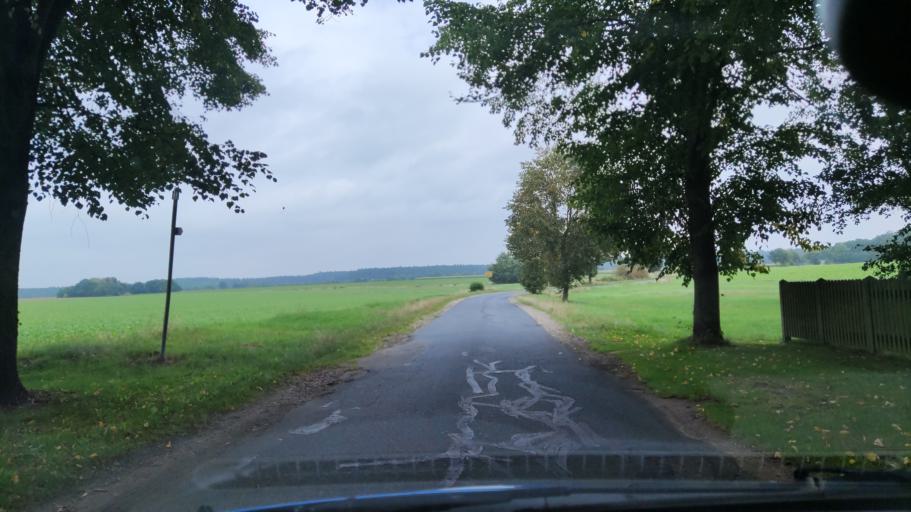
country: DE
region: Lower Saxony
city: Jelmstorf
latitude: 53.1481
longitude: 10.5382
